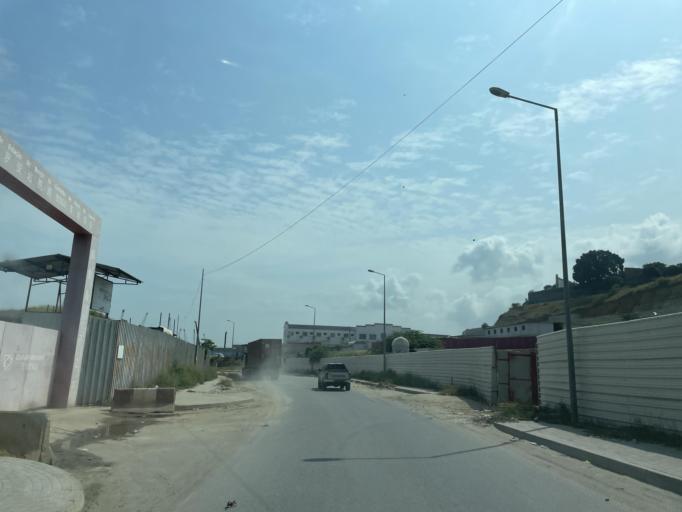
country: AO
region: Luanda
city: Luanda
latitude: -8.8062
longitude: 13.2458
